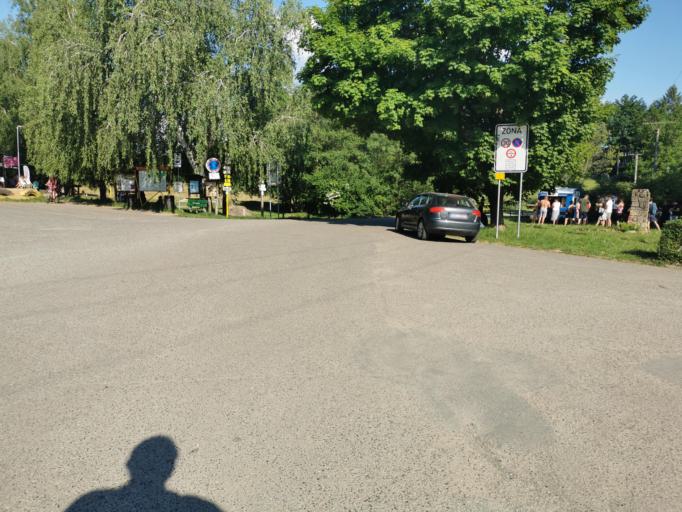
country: CZ
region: South Moravian
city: Knezdub
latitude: 48.8619
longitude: 17.3896
